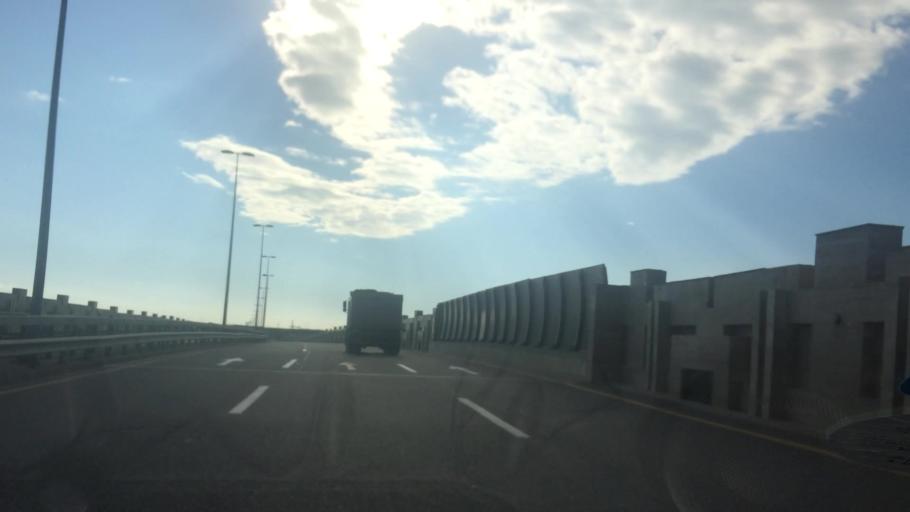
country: AZ
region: Baki
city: Hovsan
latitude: 40.3914
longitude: 50.0730
